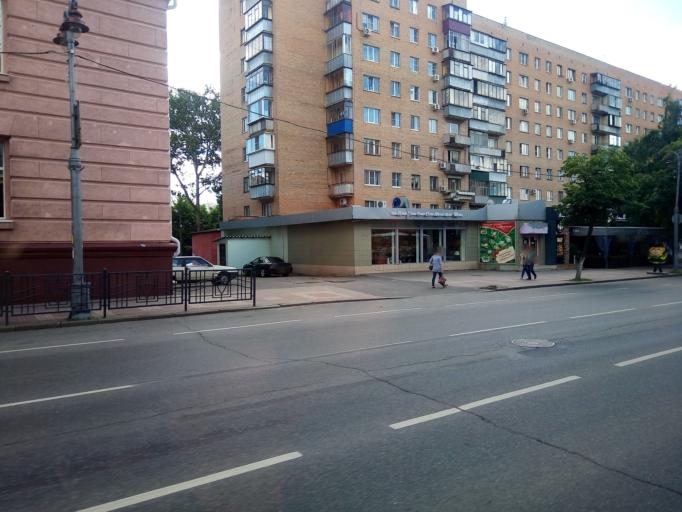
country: RU
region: Kursk
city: Kursk
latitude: 51.7382
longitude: 36.1936
